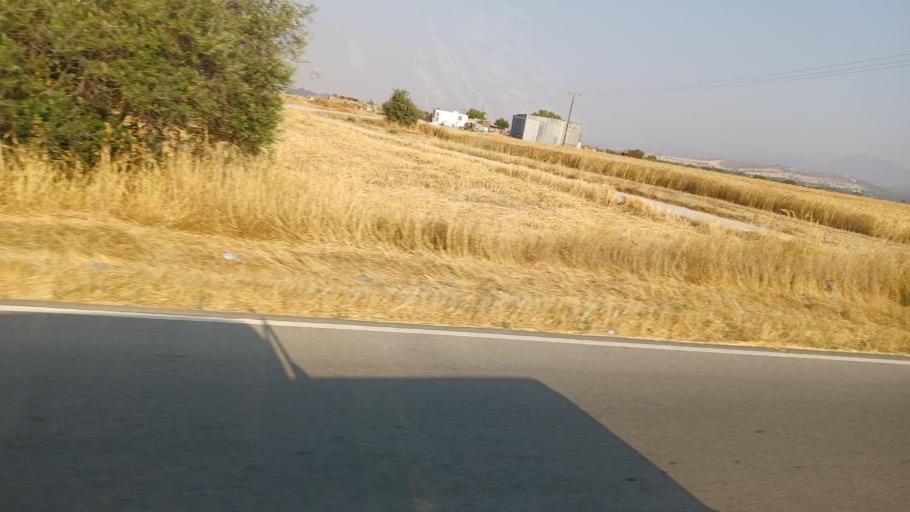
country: CY
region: Larnaka
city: Tersefanou
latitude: 34.8336
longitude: 33.5088
